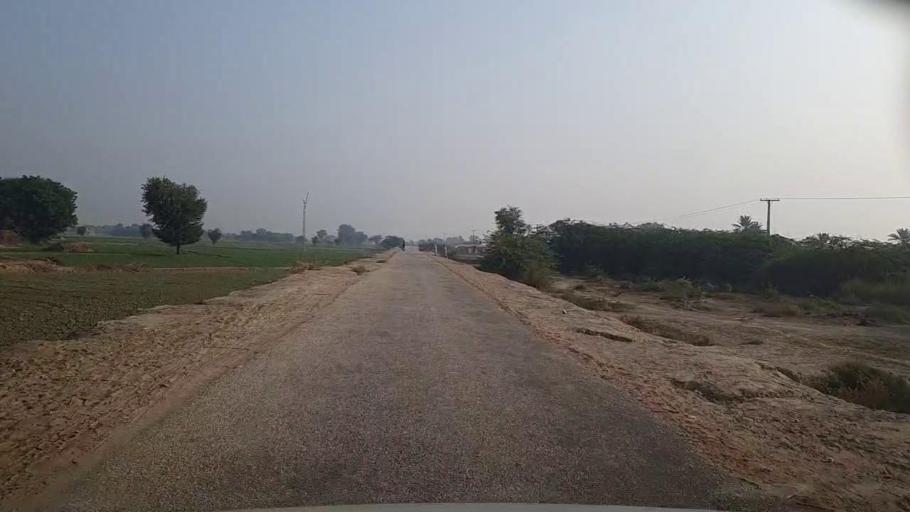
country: PK
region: Sindh
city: Kandiari
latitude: 27.0512
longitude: 68.4669
